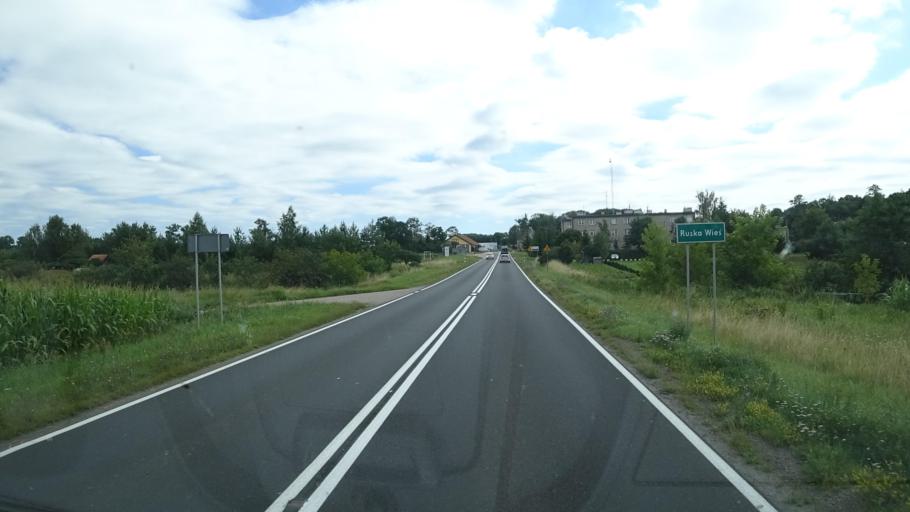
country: PL
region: Warmian-Masurian Voivodeship
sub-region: Powiat elcki
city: Stare Juchy
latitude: 53.7917
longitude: 22.1983
